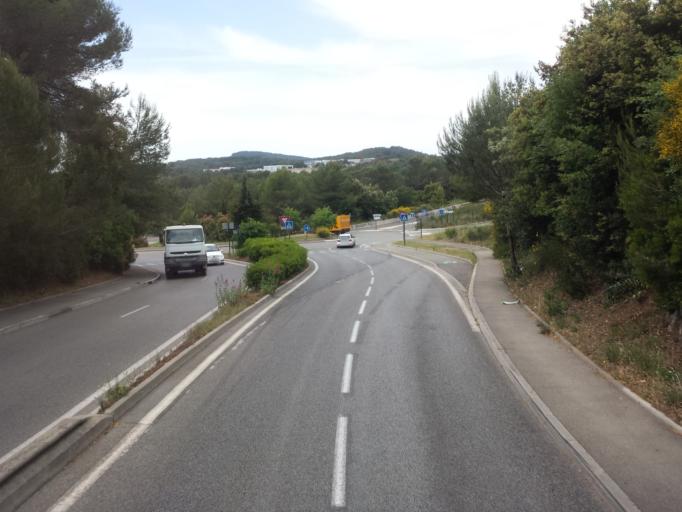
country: FR
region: Provence-Alpes-Cote d'Azur
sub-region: Departement des Alpes-Maritimes
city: Biot
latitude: 43.6128
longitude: 7.0788
